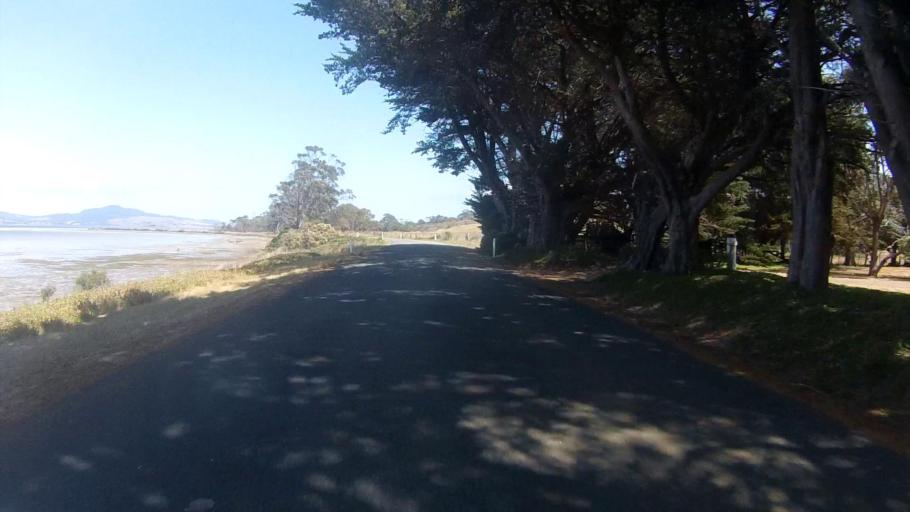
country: AU
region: Tasmania
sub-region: Sorell
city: Sorell
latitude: -42.8292
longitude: 147.8576
